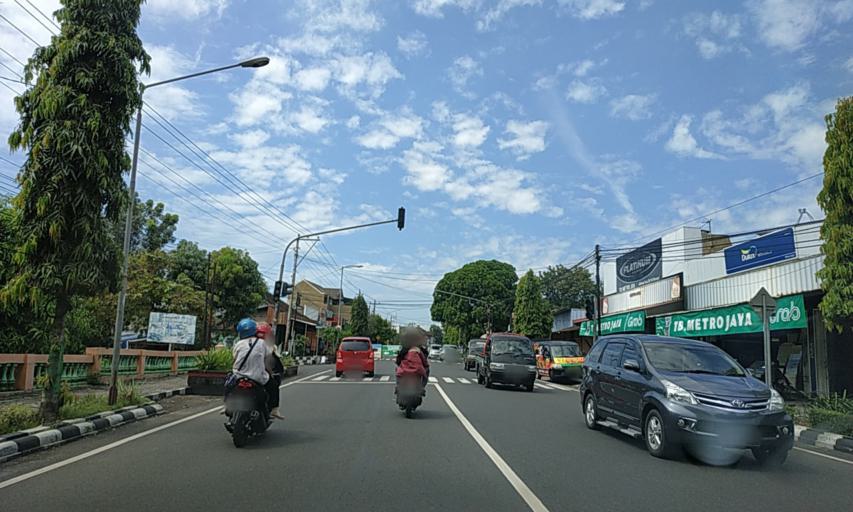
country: ID
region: Central Java
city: Selogiri
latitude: -7.8066
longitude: 110.9228
